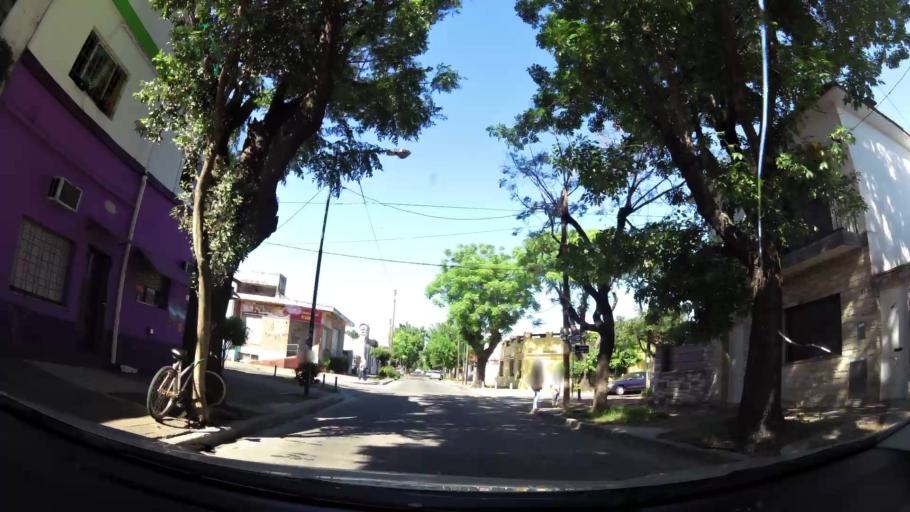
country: AR
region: Buenos Aires
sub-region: Partido de San Isidro
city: San Isidro
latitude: -34.4616
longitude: -58.5332
